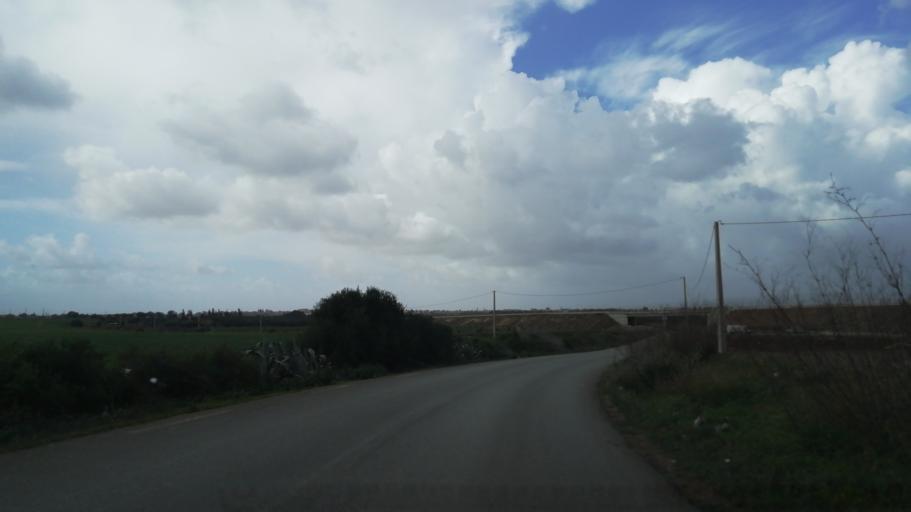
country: DZ
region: Oran
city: Sidi ech Chahmi
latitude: 35.6227
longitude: -0.5485
